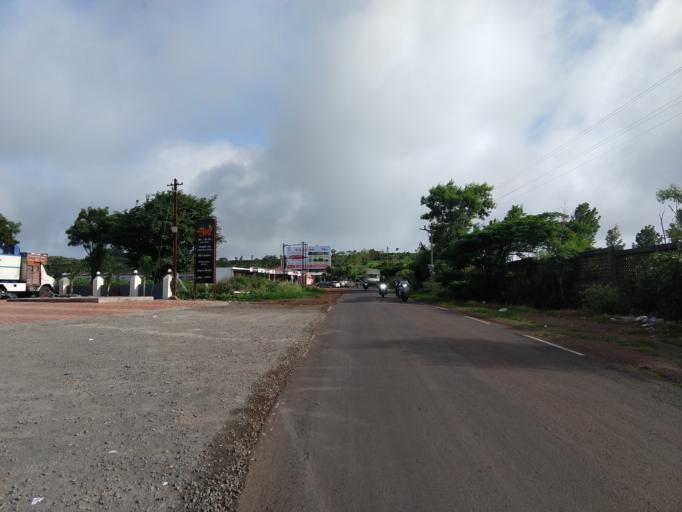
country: IN
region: Maharashtra
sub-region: Pune Division
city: Khed
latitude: 18.4013
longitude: 73.9121
